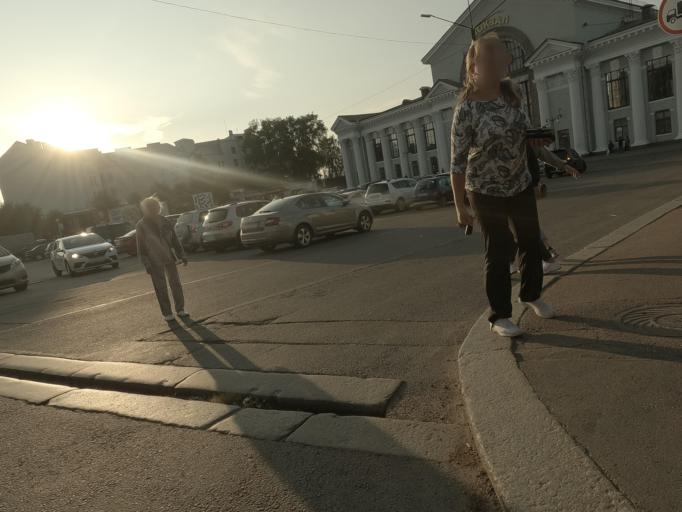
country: RU
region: Leningrad
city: Vyborg
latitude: 60.7148
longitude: 28.7516
